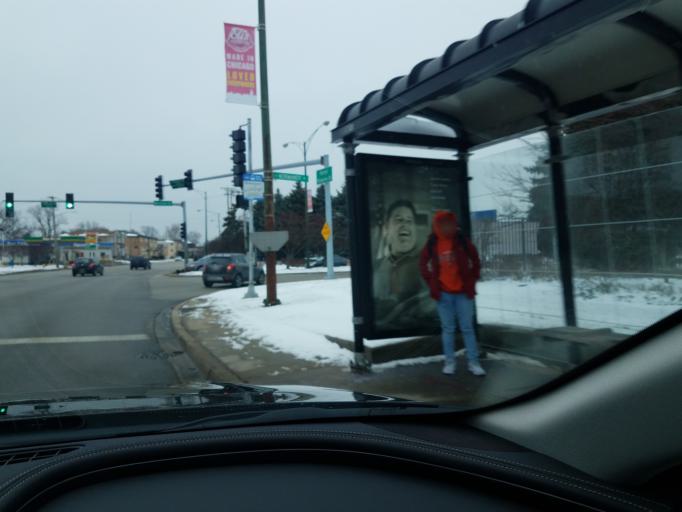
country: US
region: Illinois
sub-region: Cook County
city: Harwood Heights
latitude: 41.9599
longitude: -87.7944
